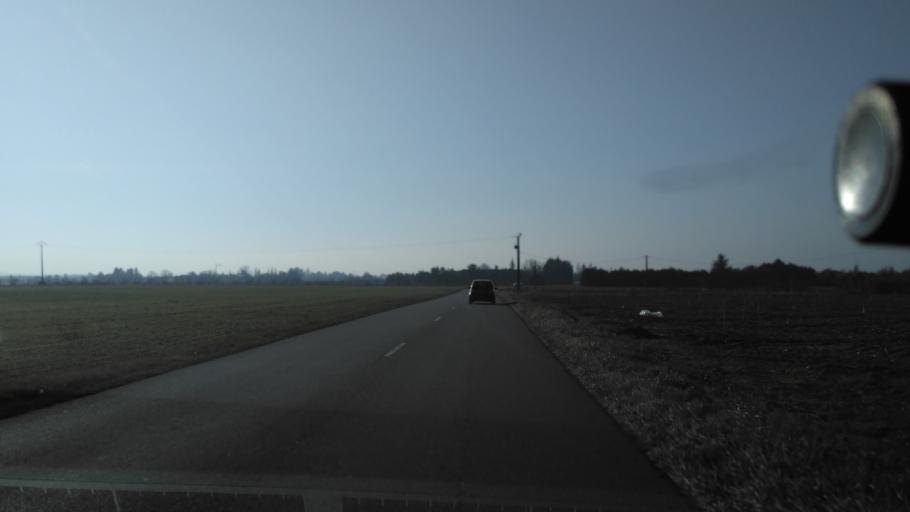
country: FR
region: Rhone-Alpes
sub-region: Departement de la Drome
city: Mours-Saint-Eusebe
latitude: 45.0682
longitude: 5.0744
